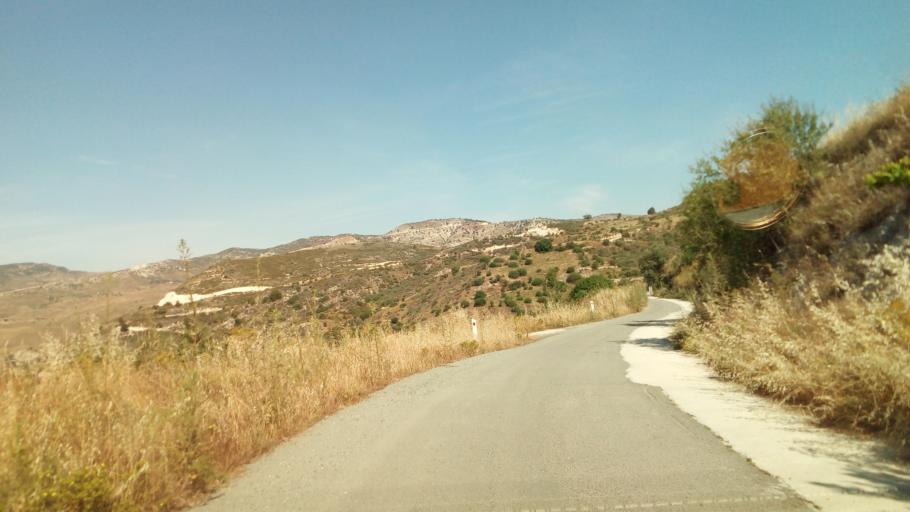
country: CY
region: Limassol
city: Pachna
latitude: 34.8151
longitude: 32.7337
